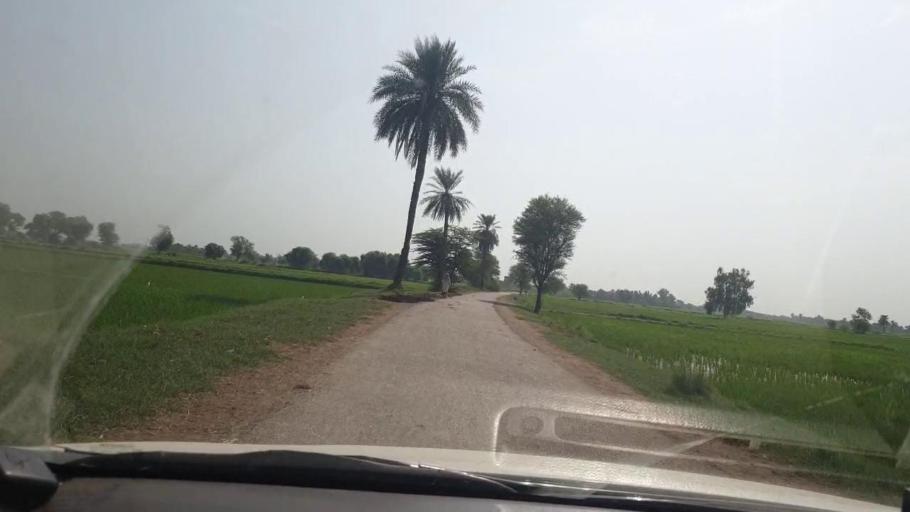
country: PK
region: Sindh
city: Chak
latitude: 27.8237
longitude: 68.7862
